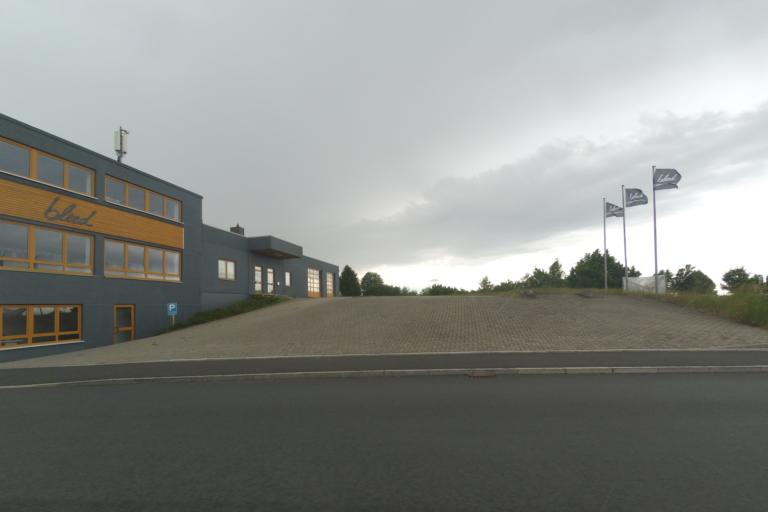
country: DE
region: Bavaria
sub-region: Upper Franconia
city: Helmbrechts
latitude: 50.2319
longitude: 11.7336
